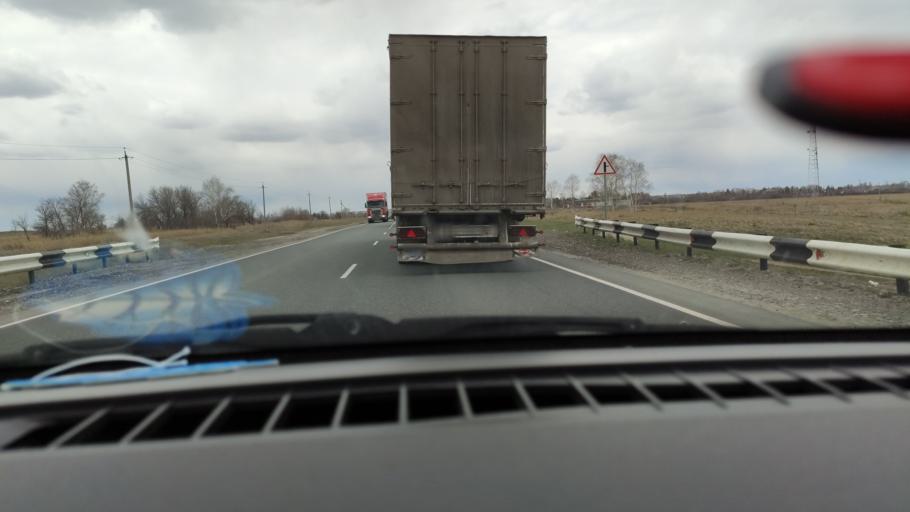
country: RU
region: Saratov
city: Sennoy
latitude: 52.1506
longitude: 46.9771
